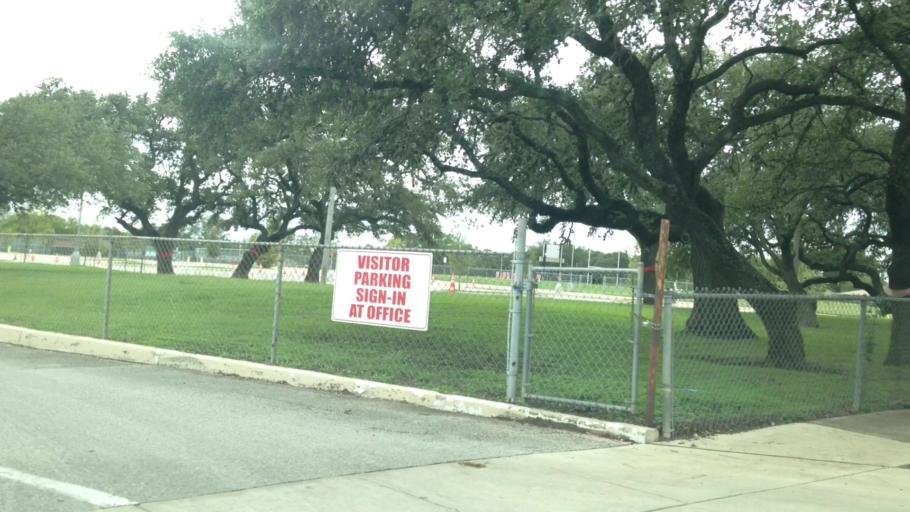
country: US
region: Texas
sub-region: Bexar County
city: Castle Hills
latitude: 29.5412
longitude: -98.5084
